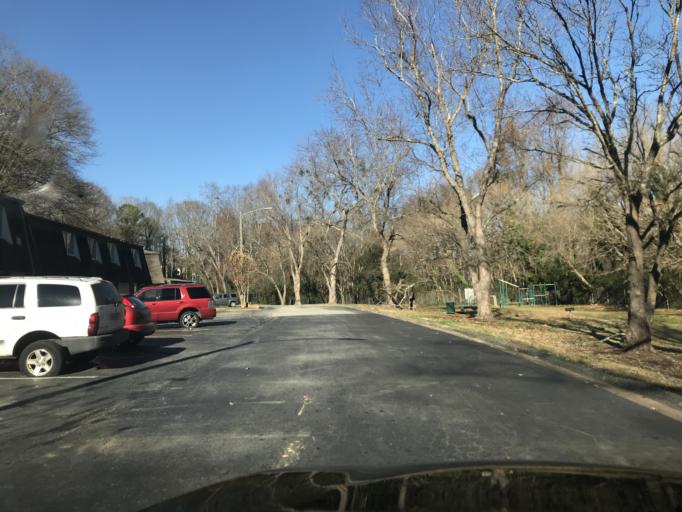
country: US
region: Georgia
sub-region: Clayton County
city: Morrow
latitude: 33.5701
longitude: -84.3643
